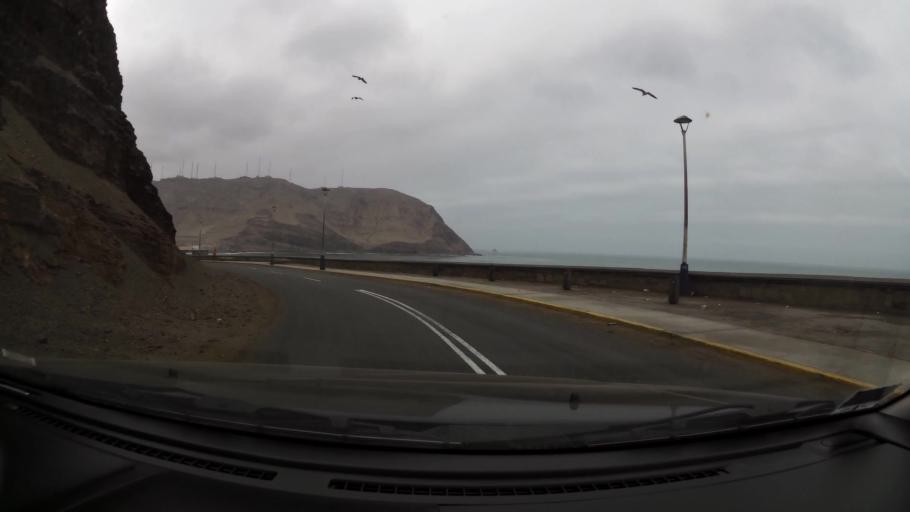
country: PE
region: Lima
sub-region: Lima
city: Surco
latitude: -12.1687
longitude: -77.0373
